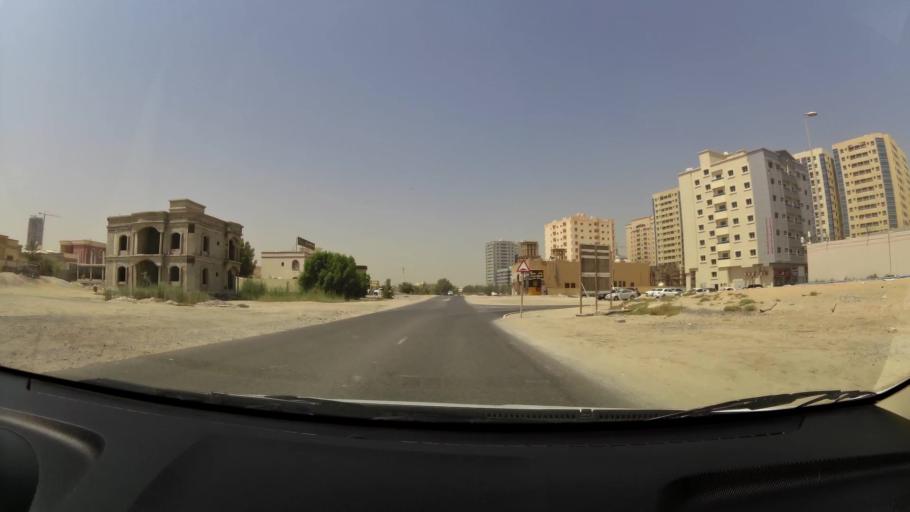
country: AE
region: Ajman
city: Ajman
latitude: 25.4053
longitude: 55.5105
